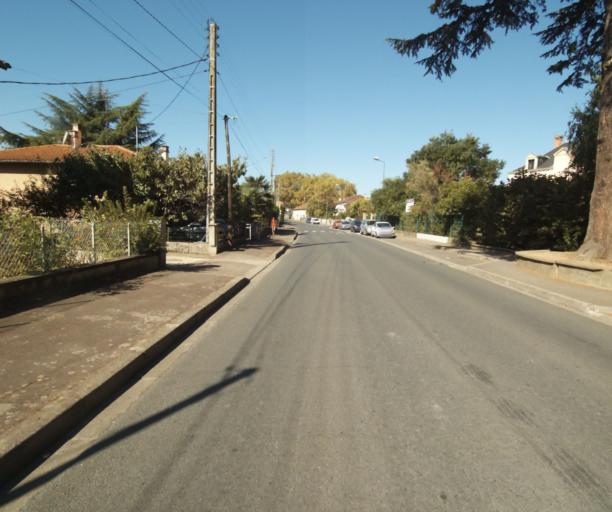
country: FR
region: Midi-Pyrenees
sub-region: Departement du Tarn-et-Garonne
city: Moissac
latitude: 44.1020
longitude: 1.0959
